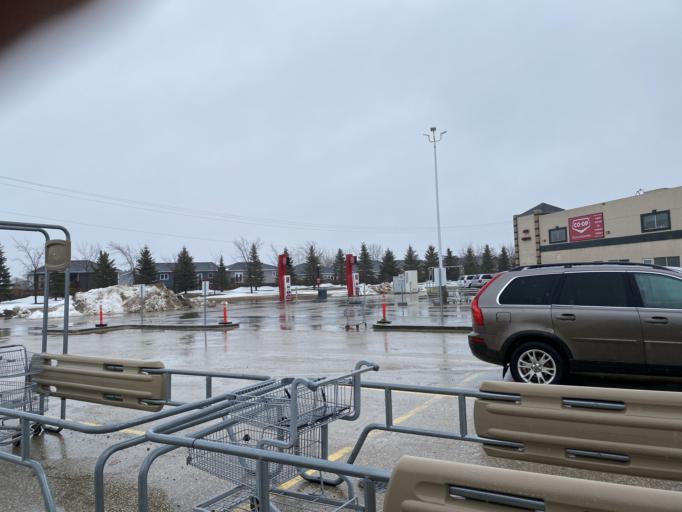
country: CA
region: Manitoba
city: Portage la Prairie
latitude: 49.9704
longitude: -98.3217
